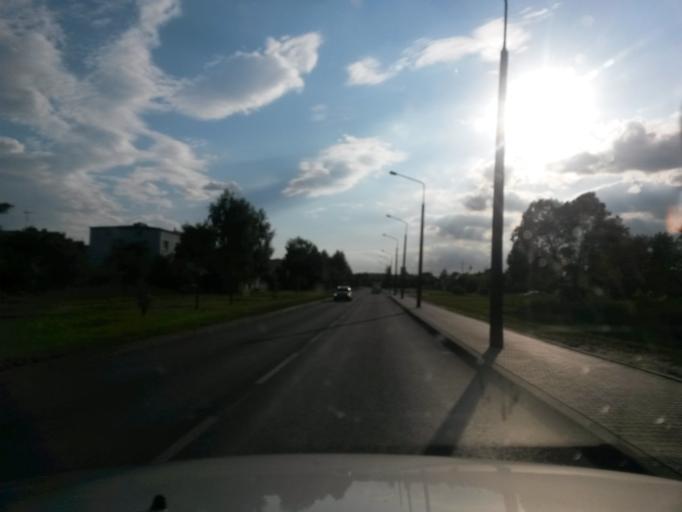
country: PL
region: Lodz Voivodeship
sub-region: Powiat belchatowski
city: Belchatow
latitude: 51.3704
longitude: 19.3639
